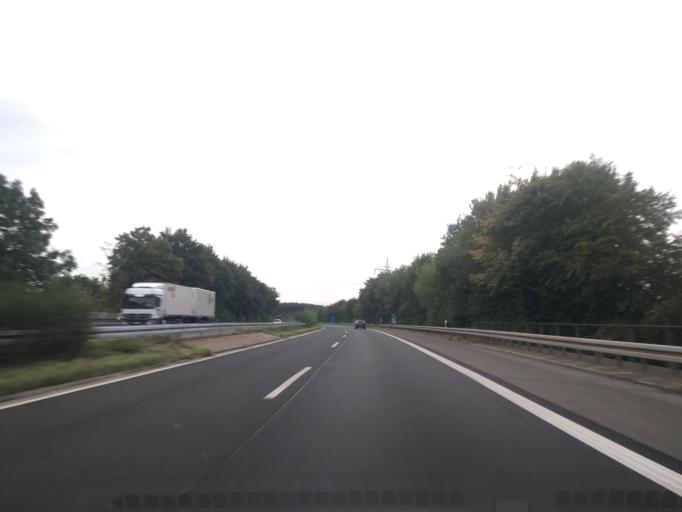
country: DE
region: North Rhine-Westphalia
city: Erkelenz
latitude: 51.0876
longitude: 6.3411
